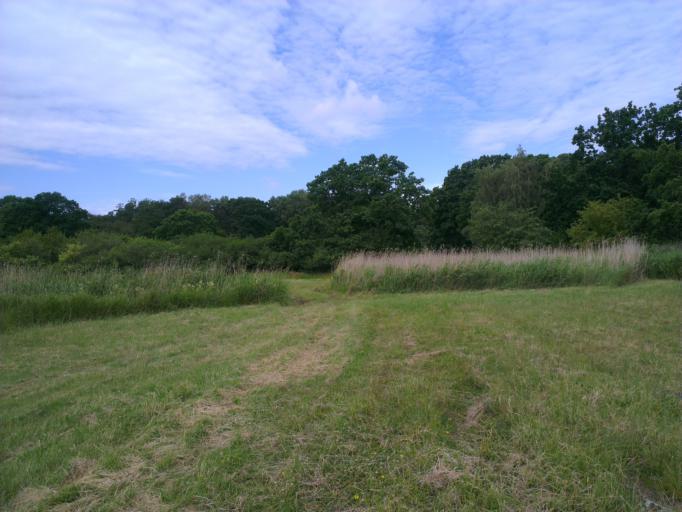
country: DK
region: Capital Region
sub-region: Frederikssund Kommune
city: Jaegerspris
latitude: 55.8968
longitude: 12.0182
